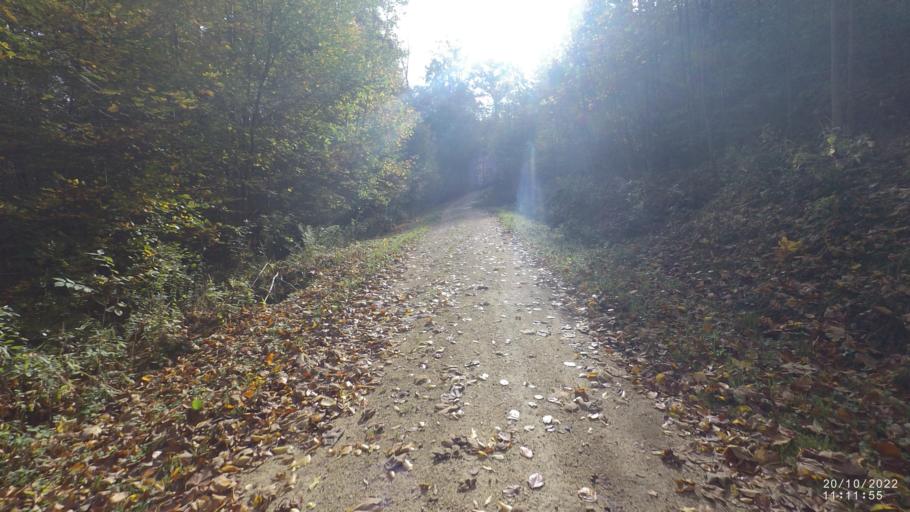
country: DE
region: Baden-Wuerttemberg
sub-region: Regierungsbezirk Stuttgart
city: Boll
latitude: 48.6238
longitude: 9.5936
